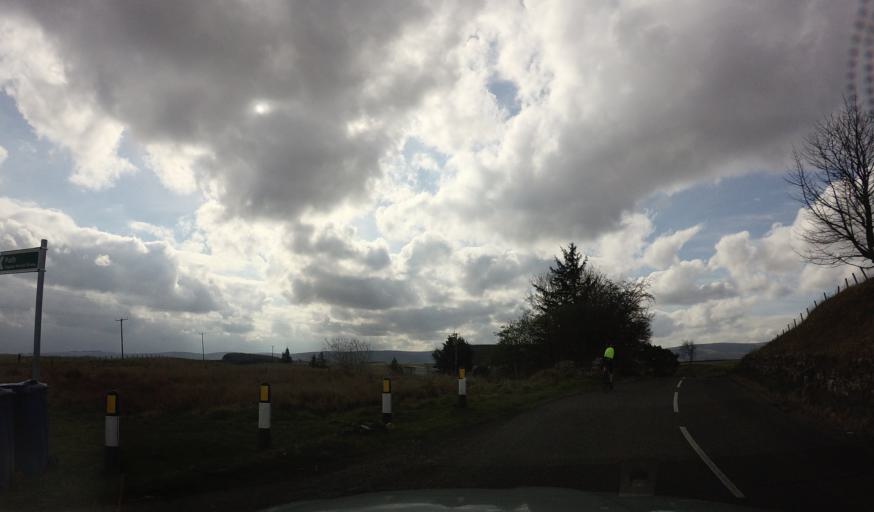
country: GB
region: Scotland
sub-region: Midlothian
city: Penicuik
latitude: 55.7989
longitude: -3.1557
